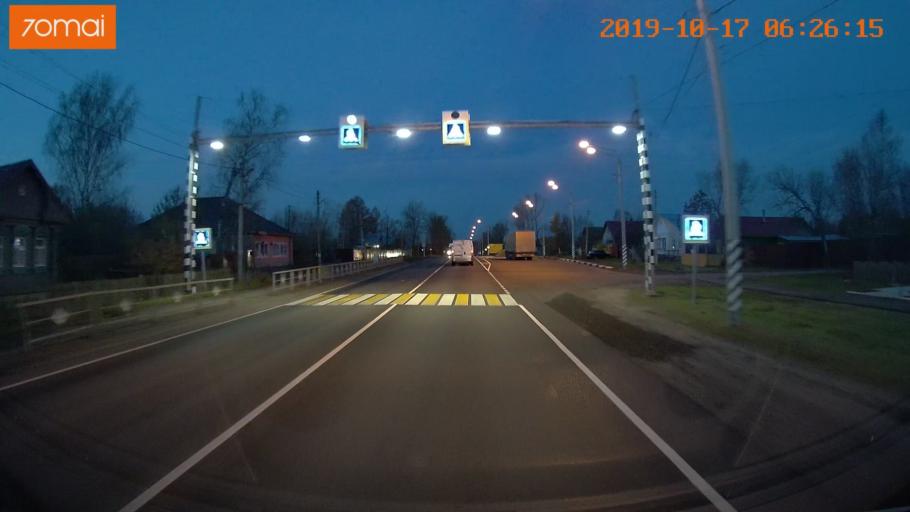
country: RU
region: Ivanovo
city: Lezhnevo
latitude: 56.7639
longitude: 40.7933
